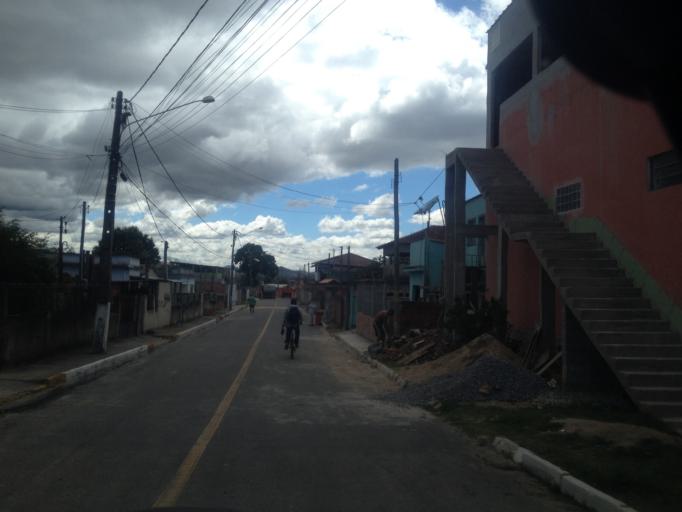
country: BR
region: Rio de Janeiro
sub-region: Porto Real
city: Porto Real
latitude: -22.4409
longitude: -44.3168
